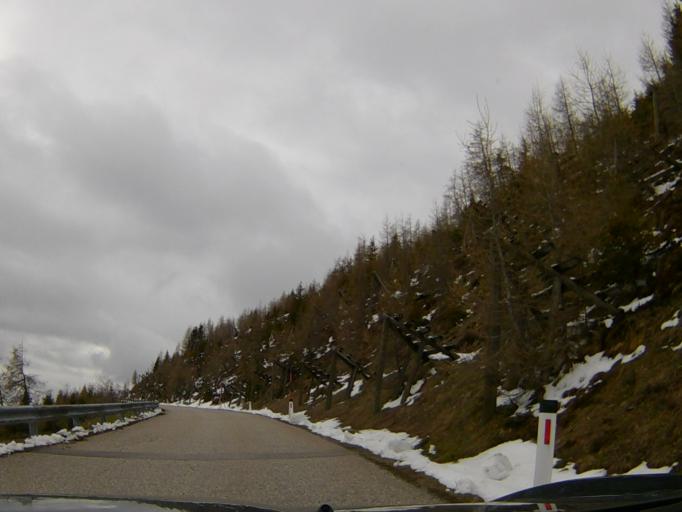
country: AT
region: Carinthia
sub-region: Politischer Bezirk Spittal an der Drau
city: Baldramsdorf
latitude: 46.7529
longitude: 13.4691
